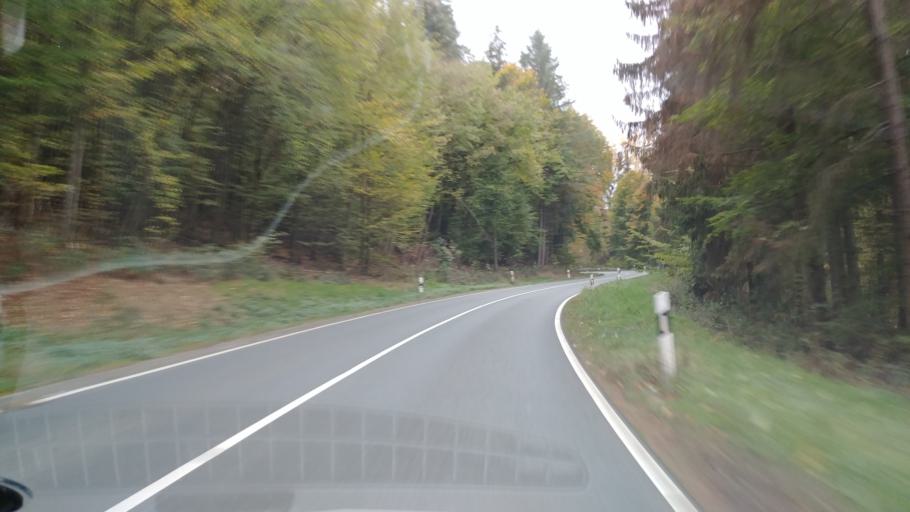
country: DE
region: Hesse
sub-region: Regierungsbezirk Darmstadt
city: Idstein
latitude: 50.2492
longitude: 8.2144
